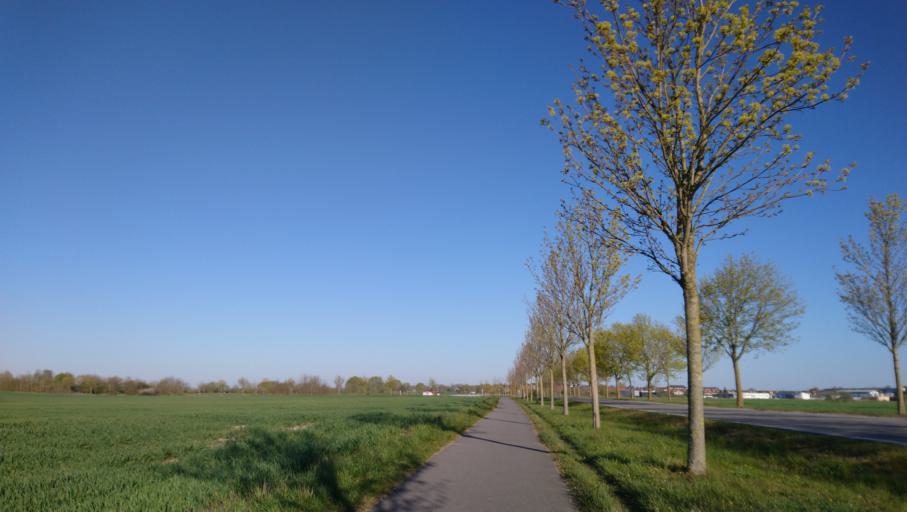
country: DE
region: Mecklenburg-Vorpommern
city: Papendorf
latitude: 54.0539
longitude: 12.1255
